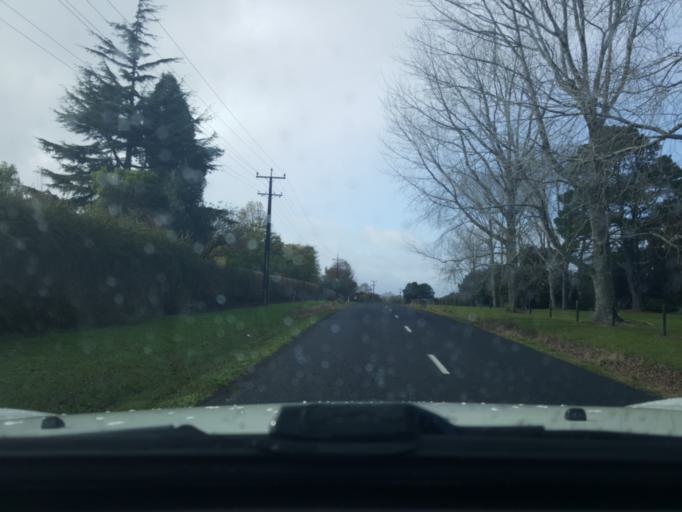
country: NZ
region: Auckland
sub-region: Auckland
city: Pukekohe East
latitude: -37.3508
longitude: 174.9877
